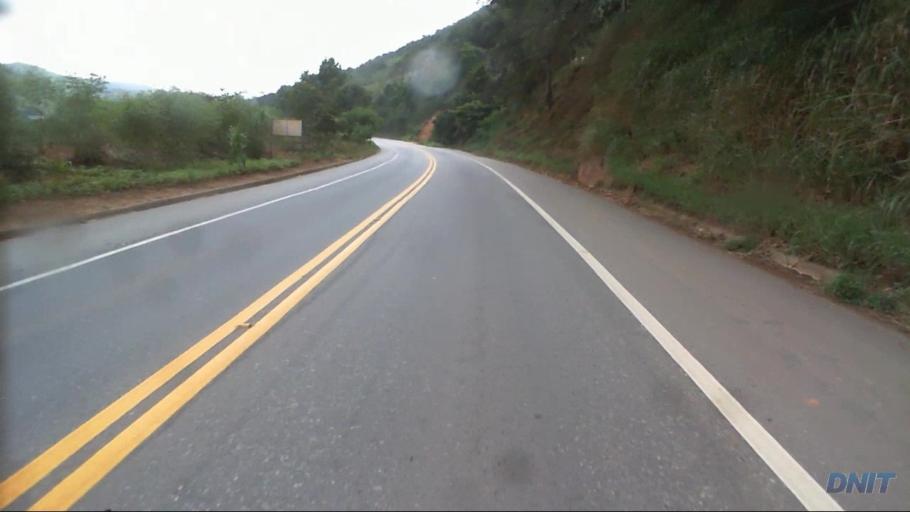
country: BR
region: Minas Gerais
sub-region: Nova Era
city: Nova Era
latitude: -19.7303
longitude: -43.0159
